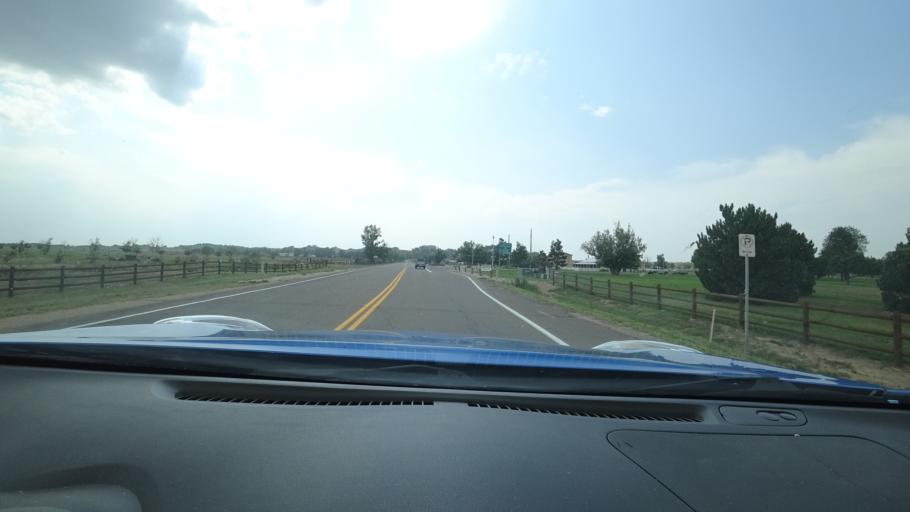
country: US
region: Colorado
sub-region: Adams County
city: Todd Creek
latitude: 39.9253
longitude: -104.8744
